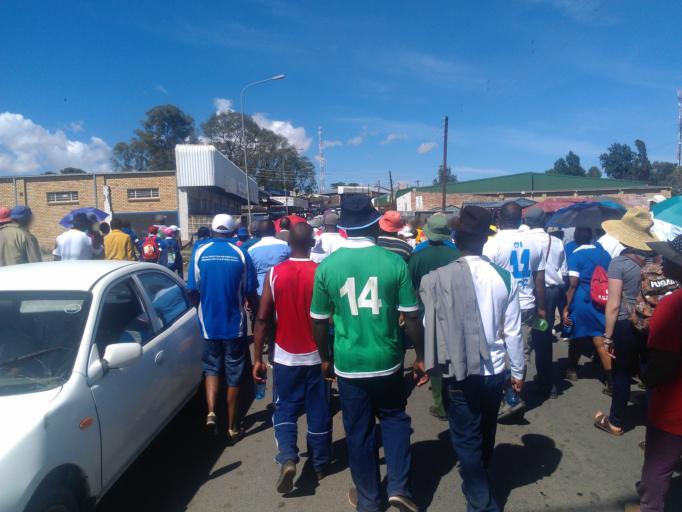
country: LS
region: Berea
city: Teyateyaneng
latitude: -29.1500
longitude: 27.7458
